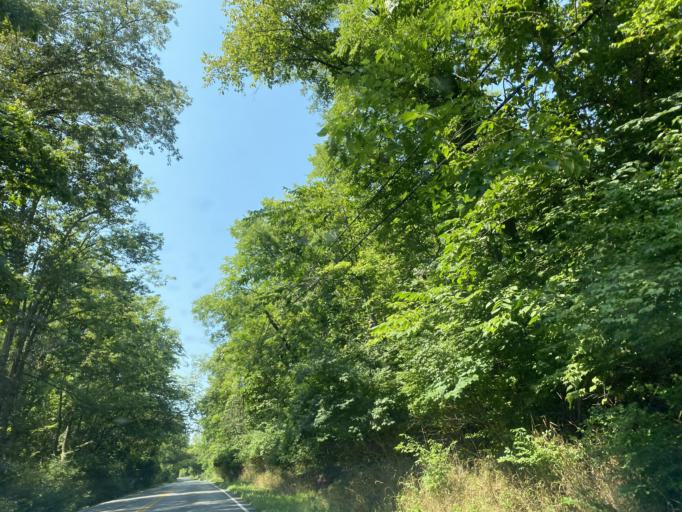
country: US
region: Kentucky
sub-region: Campbell County
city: Claryville
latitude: 38.8577
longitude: -84.4629
